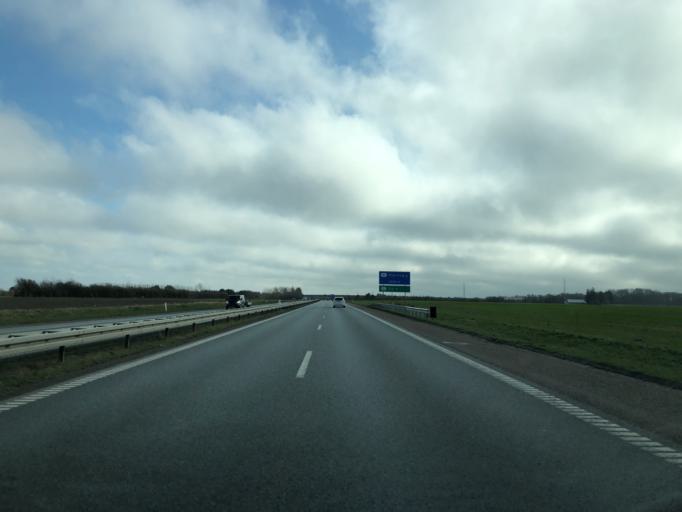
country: DK
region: North Denmark
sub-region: Hjorring Kommune
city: Hjorring
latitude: 57.4376
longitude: 10.0365
